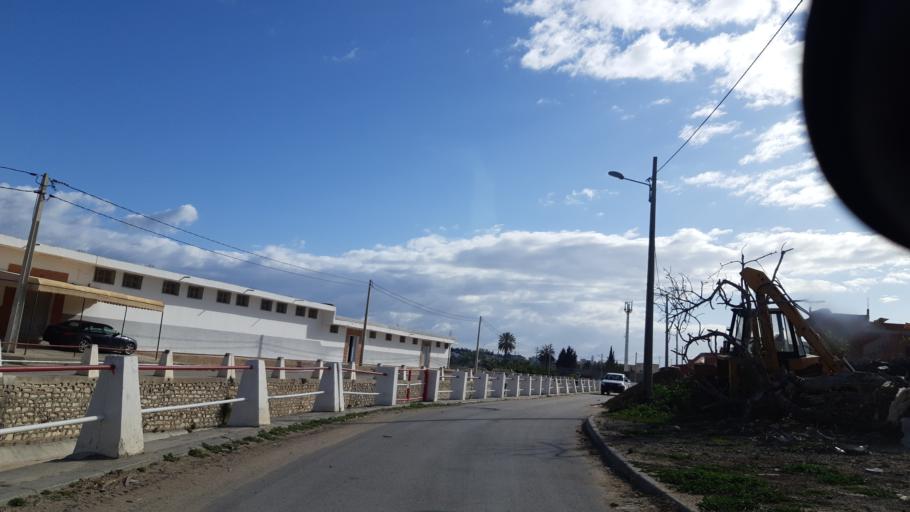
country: TN
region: Susah
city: Akouda
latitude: 35.8700
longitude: 10.5461
